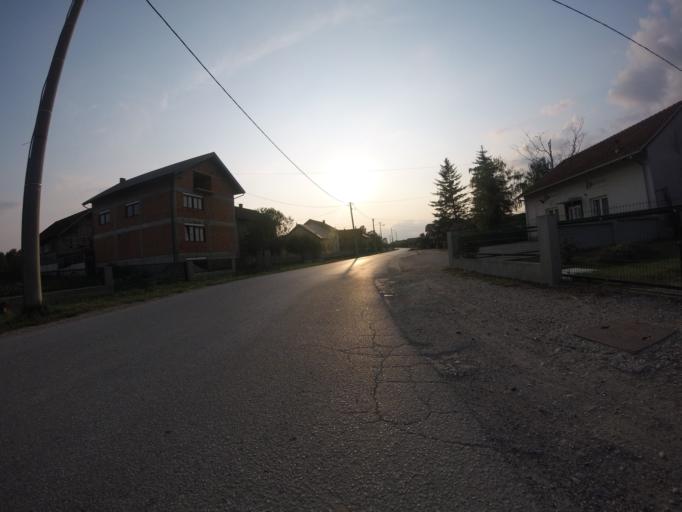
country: HR
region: Zagrebacka
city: Micevec
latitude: 45.7506
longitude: 16.1205
